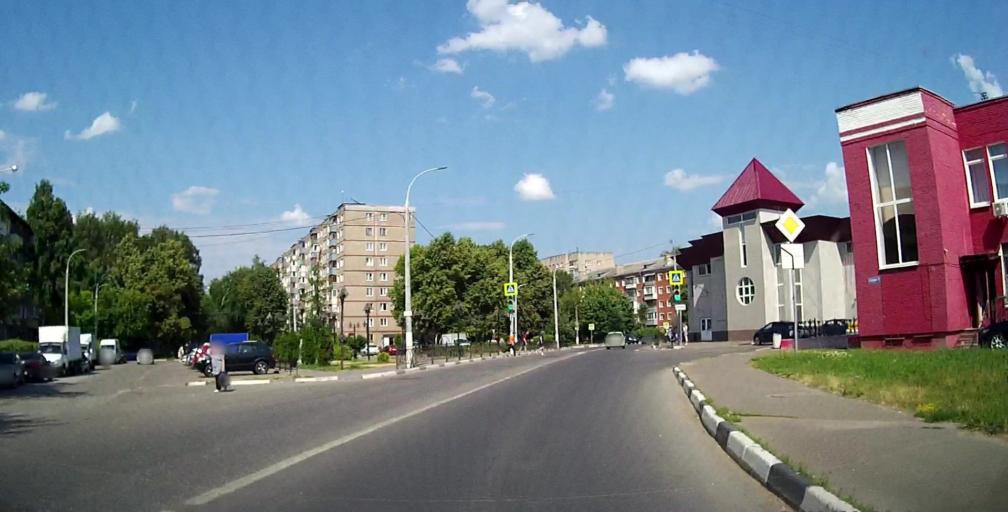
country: RU
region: Moskovskaya
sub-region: Podol'skiy Rayon
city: Podol'sk
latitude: 55.4141
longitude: 37.5276
